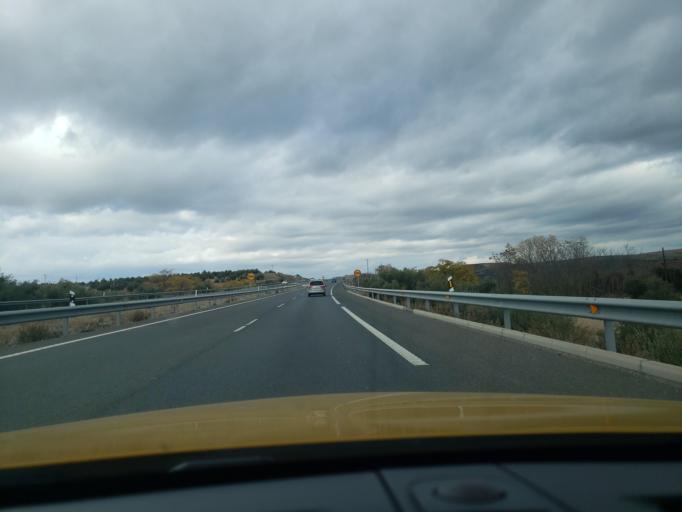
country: ES
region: Andalusia
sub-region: Provincia de Jaen
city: Jaen
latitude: 37.8567
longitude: -3.7650
